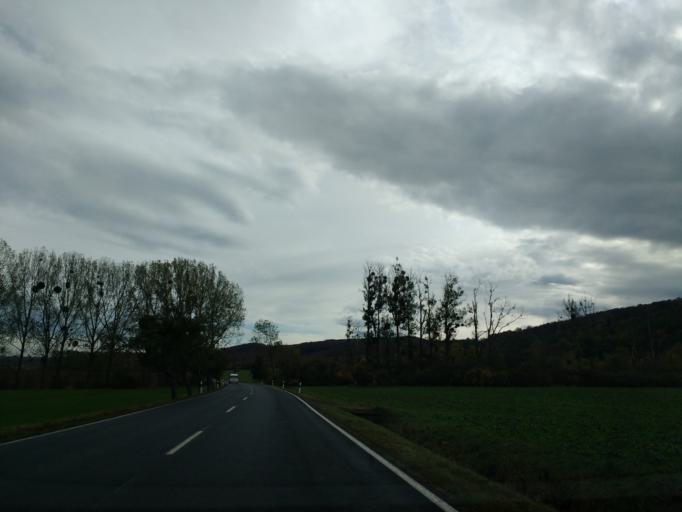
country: DE
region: Thuringia
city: Deuna
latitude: 51.3480
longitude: 10.4530
